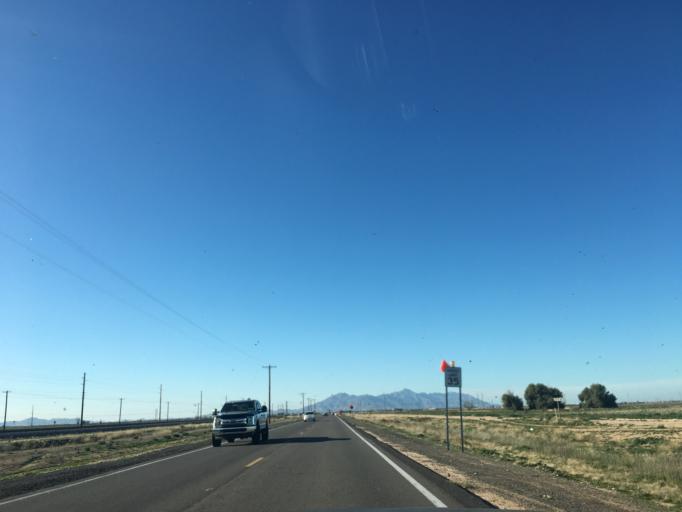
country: US
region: Arizona
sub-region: Pinal County
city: Maricopa
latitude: 33.0189
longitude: -111.9867
